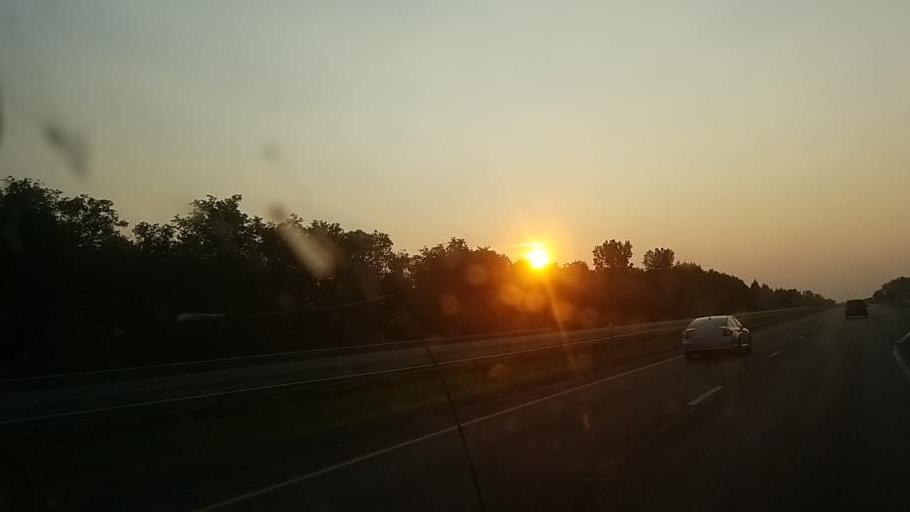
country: US
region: New York
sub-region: Herkimer County
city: Frankfort
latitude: 43.0732
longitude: -75.0984
